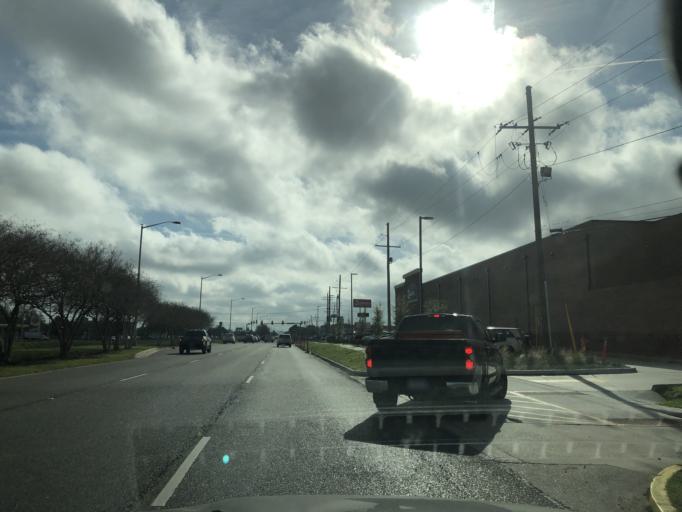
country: US
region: Louisiana
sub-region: Jefferson Parish
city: Metairie Terrace
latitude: 30.0057
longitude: -90.1970
